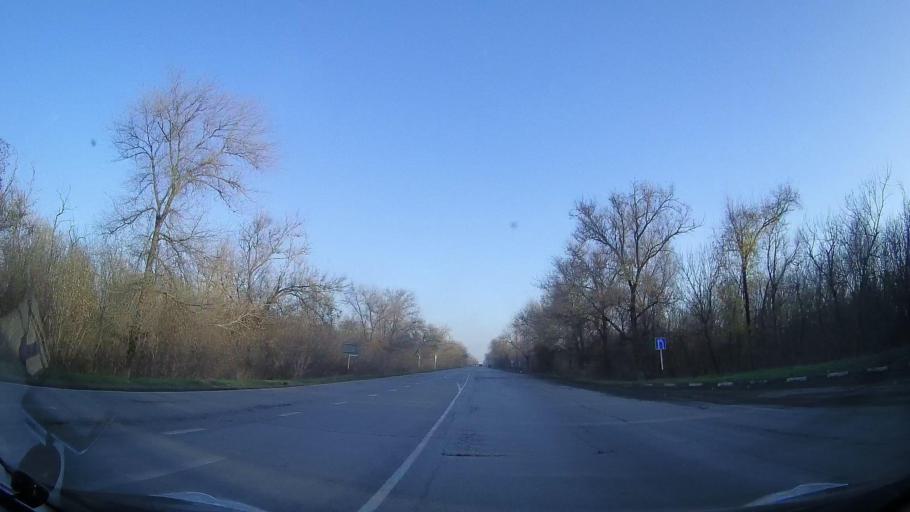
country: RU
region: Rostov
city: Bataysk
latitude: 47.0477
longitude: 39.8434
